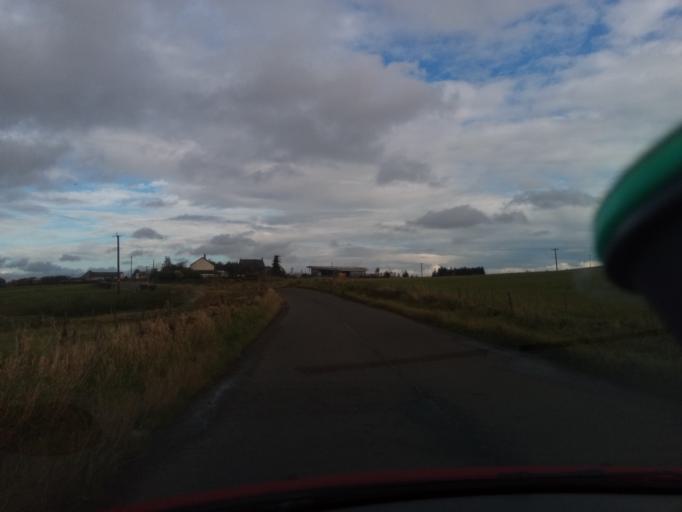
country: GB
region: Scotland
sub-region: South Lanarkshire
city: Carnwath
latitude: 55.7665
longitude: -3.6039
